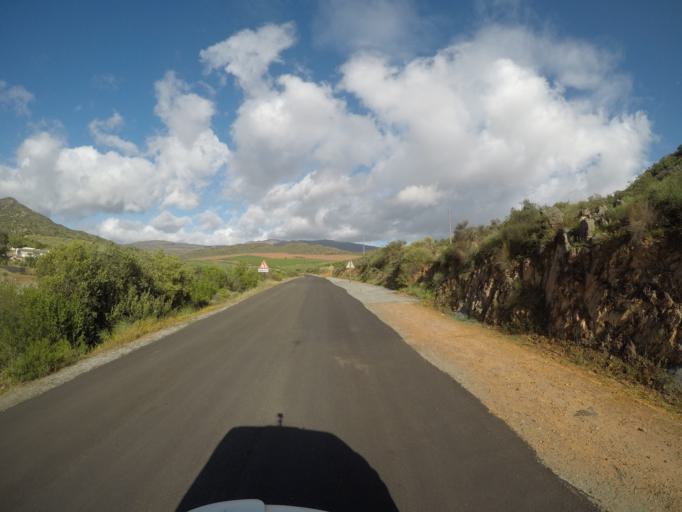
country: ZA
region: Western Cape
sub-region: West Coast District Municipality
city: Clanwilliam
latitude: -32.4300
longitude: 18.9538
